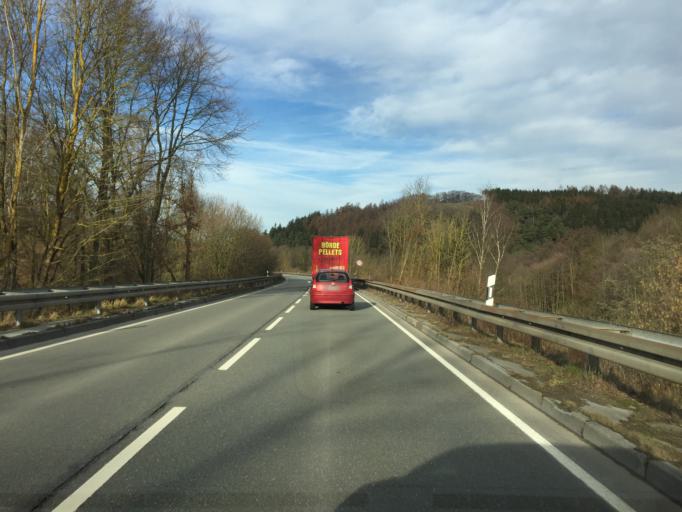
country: DE
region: North Rhine-Westphalia
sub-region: Regierungsbezirk Arnsberg
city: Ruthen
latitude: 51.4522
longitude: 8.4362
